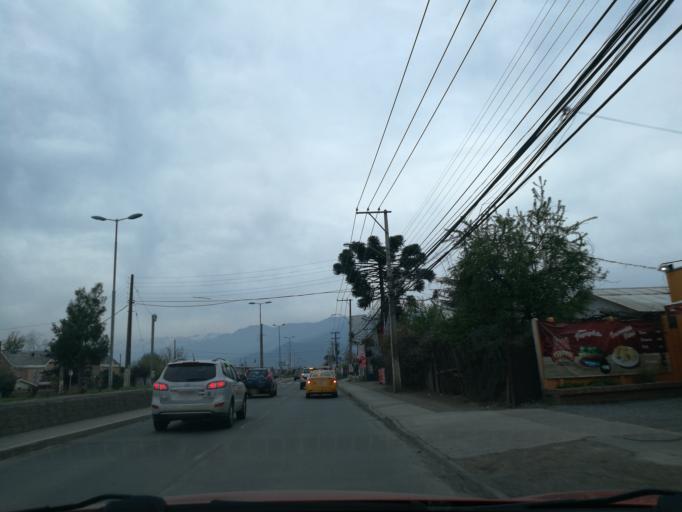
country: CL
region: O'Higgins
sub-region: Provincia de Cachapoal
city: Machali
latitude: -34.1759
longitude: -70.6942
